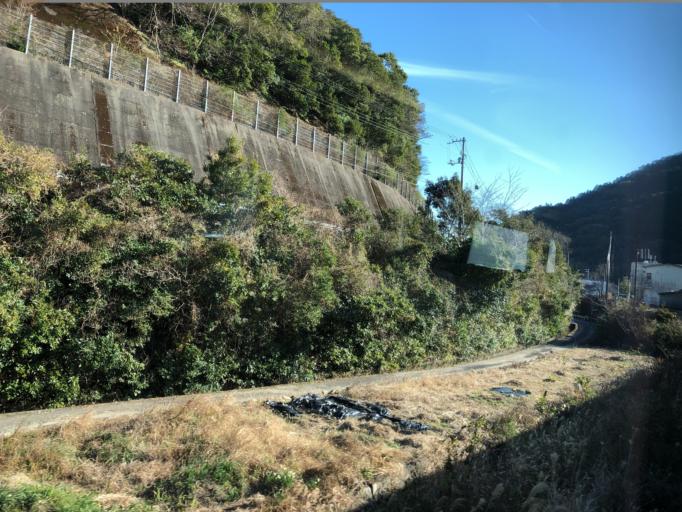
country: JP
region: Kochi
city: Nakamura
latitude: 33.0824
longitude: 133.1016
